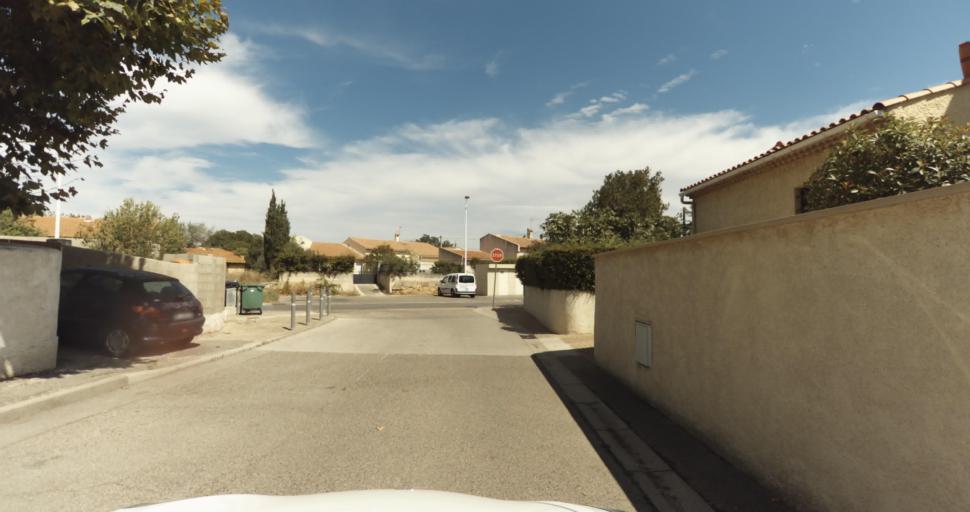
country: FR
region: Provence-Alpes-Cote d'Azur
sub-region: Departement des Bouches-du-Rhone
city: Miramas
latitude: 43.5839
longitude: 5.0117
